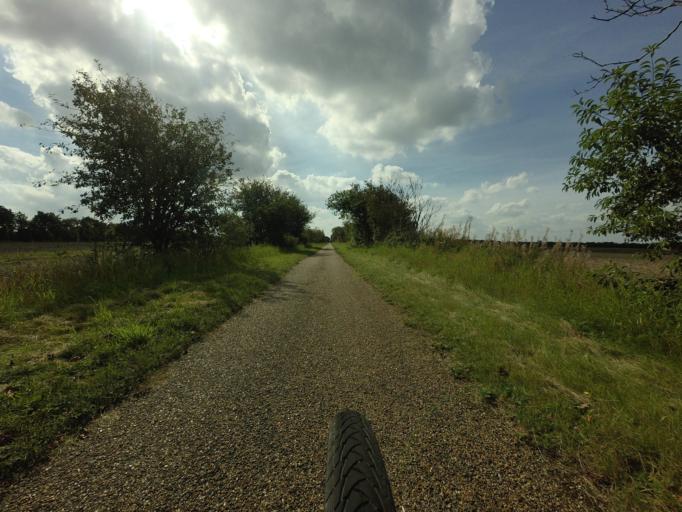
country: DK
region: Central Jutland
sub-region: Herning Kommune
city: Sunds
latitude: 56.2199
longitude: 9.0587
